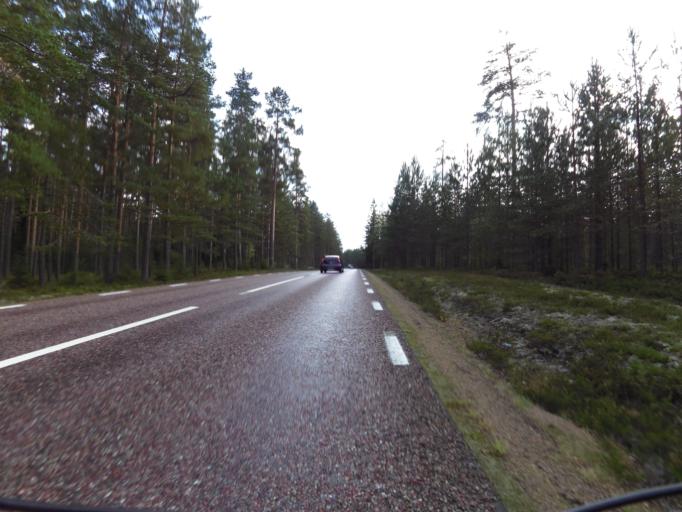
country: SE
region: Gaevleborg
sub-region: Ockelbo Kommun
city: Ockelbo
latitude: 60.8125
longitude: 16.7049
